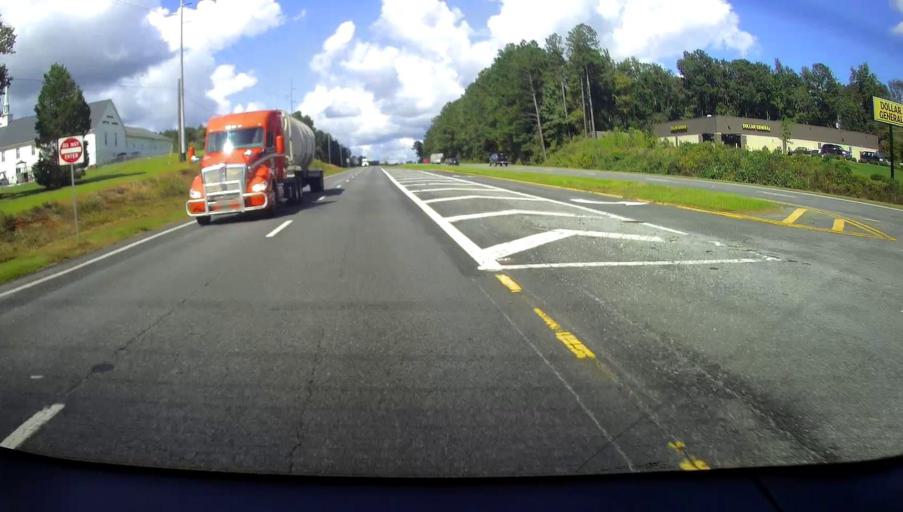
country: US
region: Georgia
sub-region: Jones County
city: Gray
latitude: 32.9624
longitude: -83.5811
